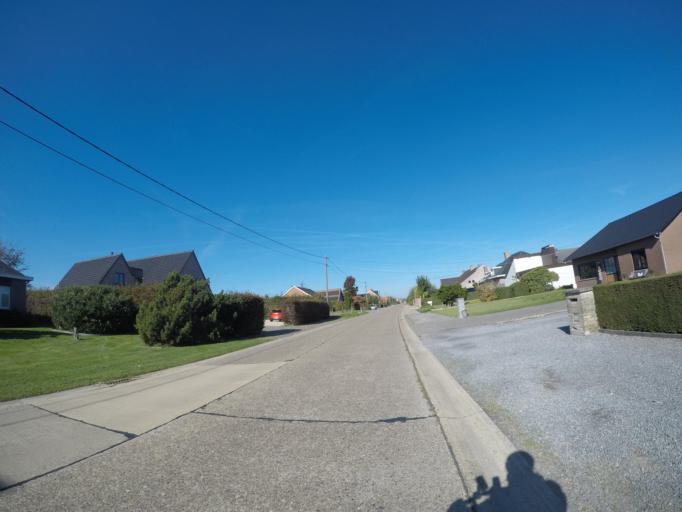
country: BE
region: Flanders
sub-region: Provincie Limburg
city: Alken
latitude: 50.8597
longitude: 5.2960
